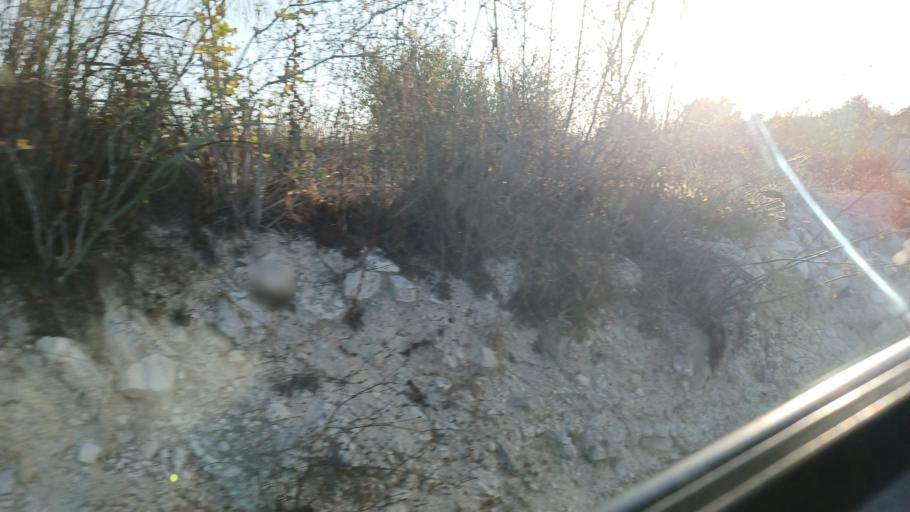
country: CY
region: Pafos
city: Mesogi
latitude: 34.8569
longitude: 32.4901
